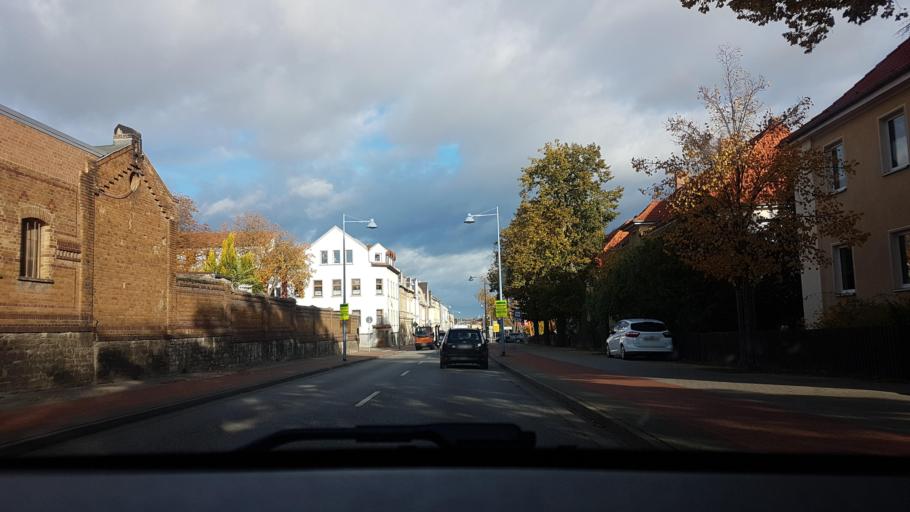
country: DE
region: Saxony-Anhalt
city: Bernburg
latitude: 51.7941
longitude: 11.7518
